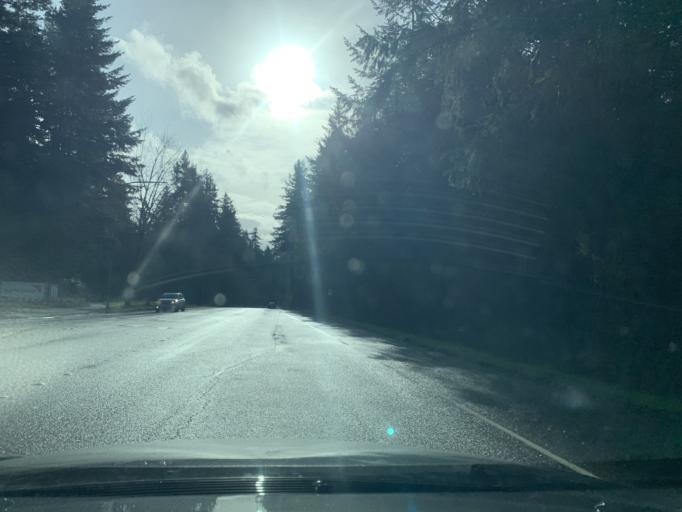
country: US
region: Washington
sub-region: King County
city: Lakeland South
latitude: 47.2905
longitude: -122.2922
